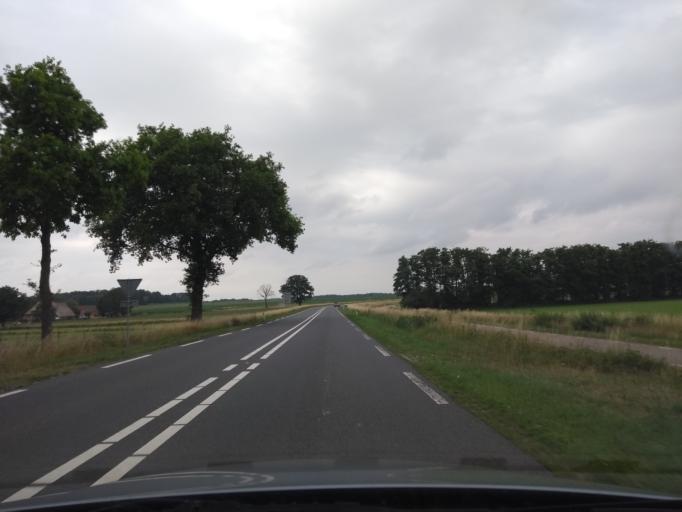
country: NL
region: Overijssel
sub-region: Gemeente Hof van Twente
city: Markelo
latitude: 52.2602
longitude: 6.5295
